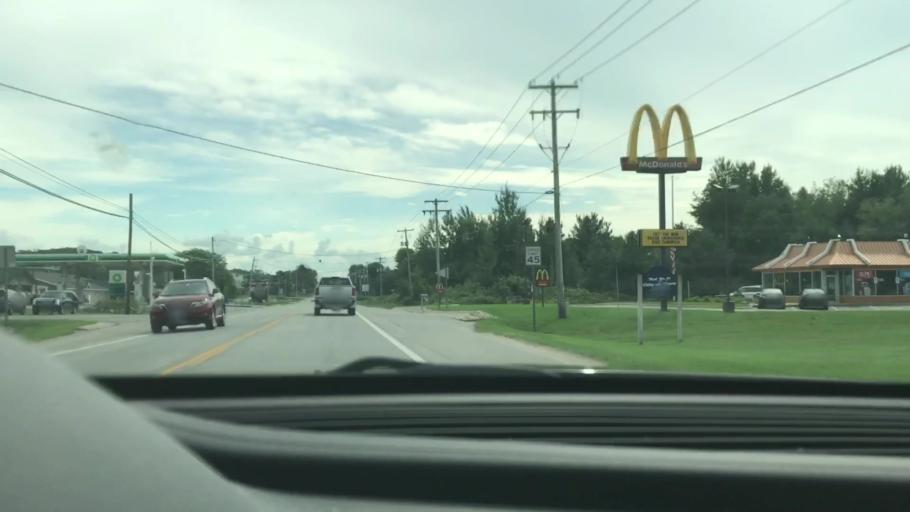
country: US
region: Michigan
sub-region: Antrim County
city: Bellaire
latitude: 44.9741
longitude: -85.1984
